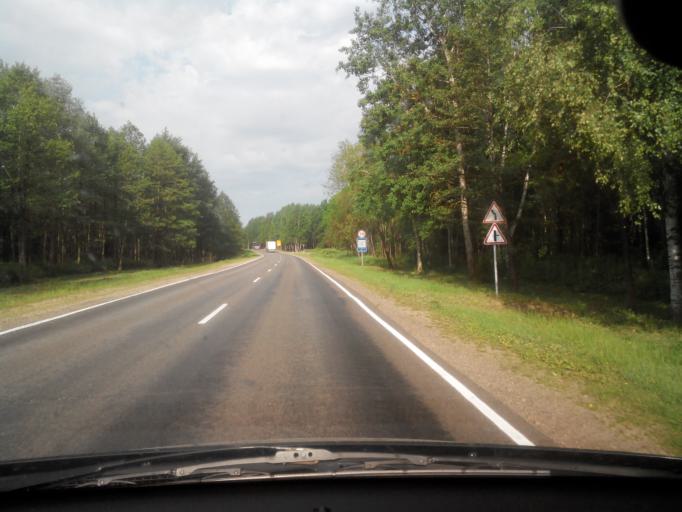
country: BY
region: Minsk
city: Myadzyel
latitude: 55.0618
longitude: 27.1530
